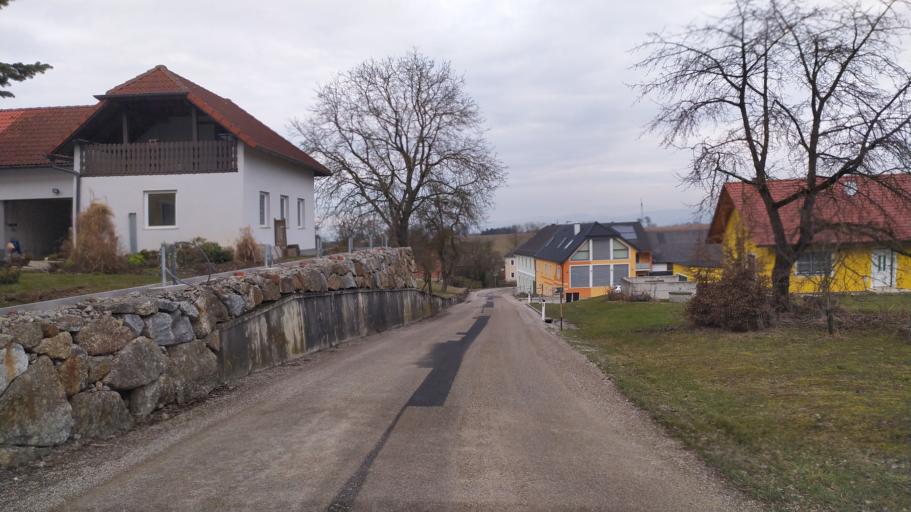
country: AT
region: Lower Austria
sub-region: Politischer Bezirk Amstetten
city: Strengberg
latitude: 48.1364
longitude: 14.7156
